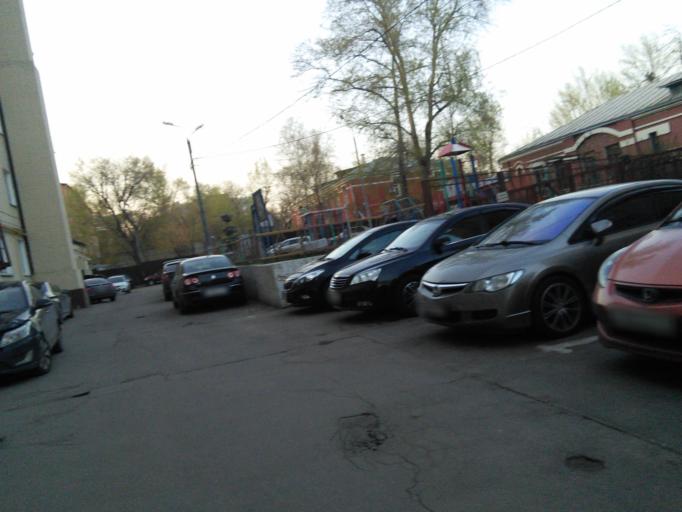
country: RU
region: Moscow
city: Kotlovka
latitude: 55.6929
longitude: 37.6229
